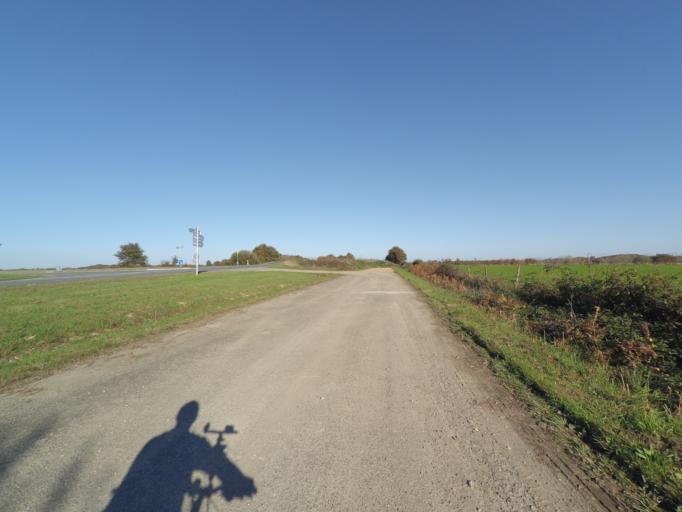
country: FR
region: Pays de la Loire
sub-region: Departement de la Loire-Atlantique
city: La Planche
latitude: 46.9928
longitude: -1.3845
